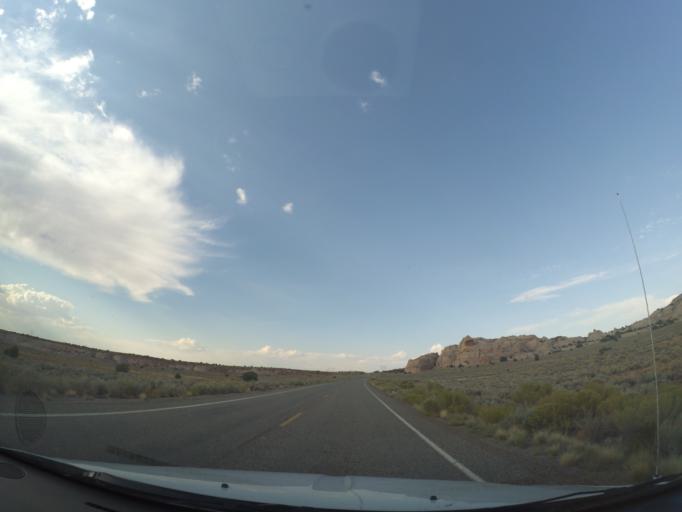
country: US
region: Arizona
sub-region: Coconino County
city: LeChee
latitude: 36.6990
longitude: -111.4444
